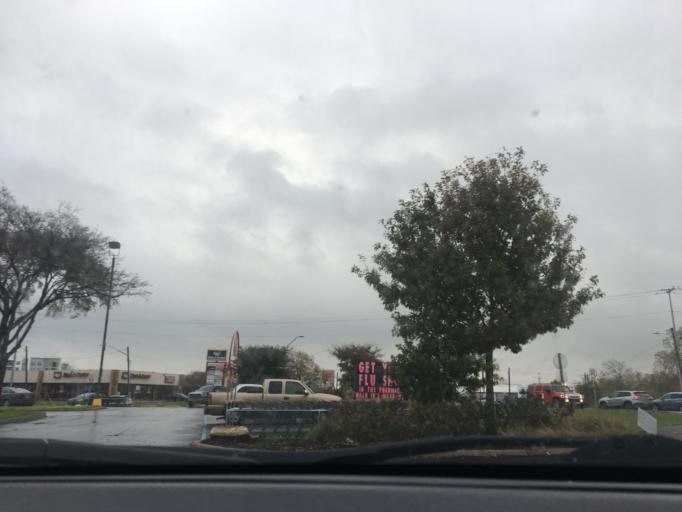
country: US
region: Texas
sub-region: Hays County
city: San Marcos
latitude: 29.8860
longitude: -97.9264
